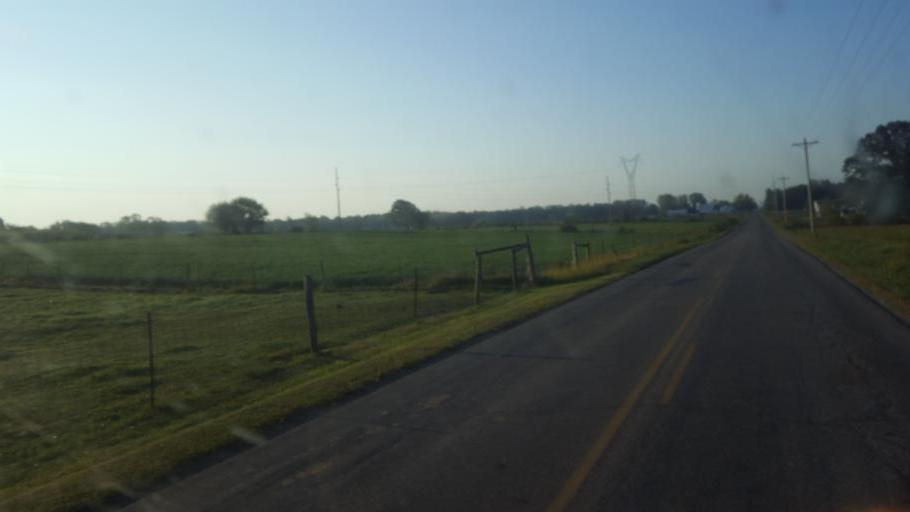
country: US
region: Indiana
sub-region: LaGrange County
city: Lagrange
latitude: 41.6153
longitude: -85.4244
